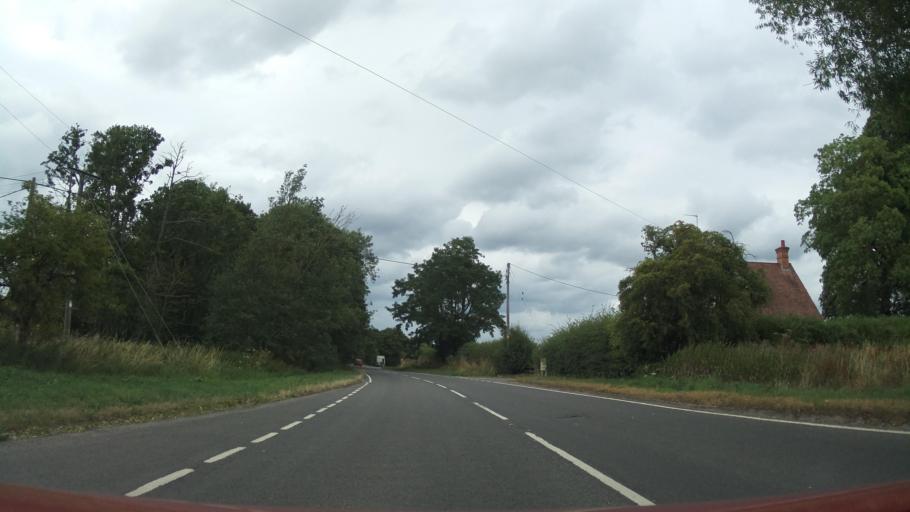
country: GB
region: England
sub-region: Leicestershire
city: Castle Donington
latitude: 52.8083
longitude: -1.3769
